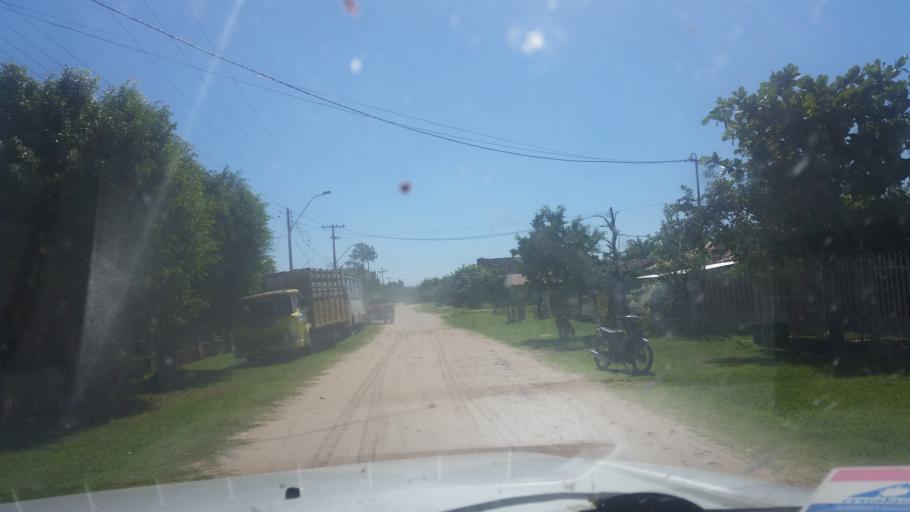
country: PY
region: Neembucu
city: Pilar
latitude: -26.8194
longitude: -57.9815
